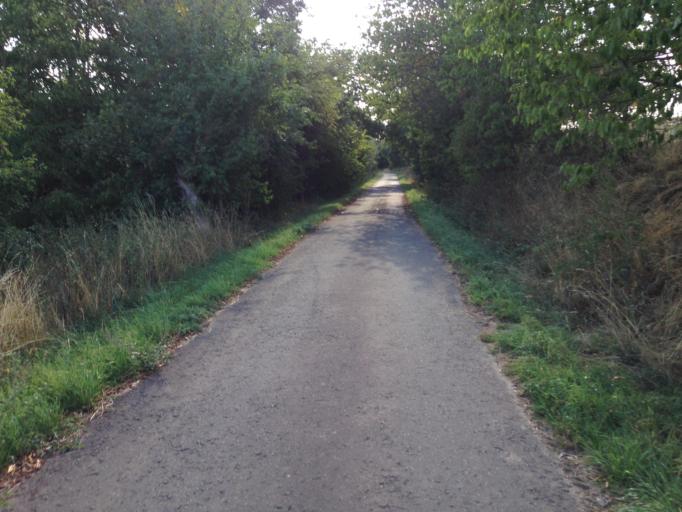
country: DE
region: Hesse
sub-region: Regierungsbezirk Giessen
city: Reiskirchen
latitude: 50.6224
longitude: 8.8599
